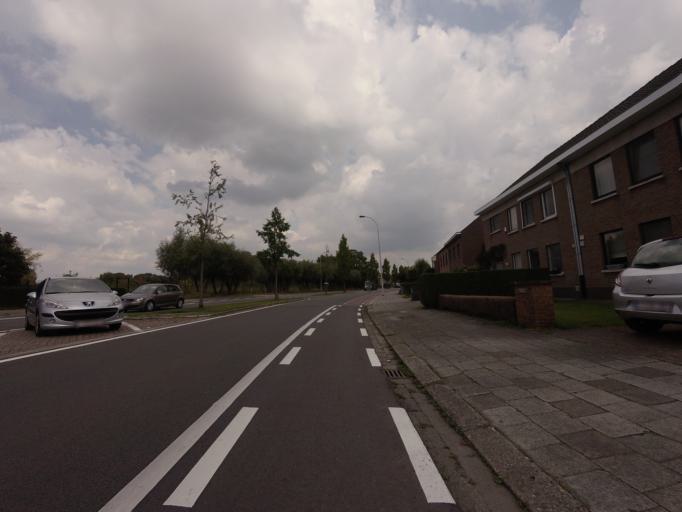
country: BE
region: Flanders
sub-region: Provincie Antwerpen
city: Aartselaar
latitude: 51.1575
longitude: 4.3975
